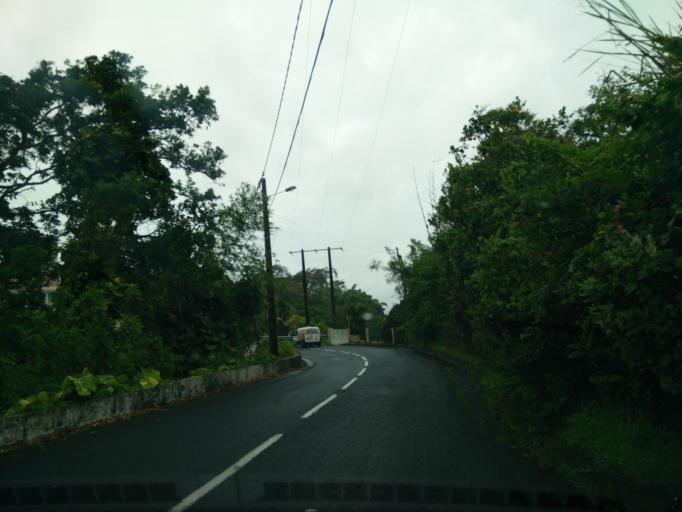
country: MQ
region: Martinique
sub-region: Martinique
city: Saint-Joseph
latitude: 14.6595
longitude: -61.0853
